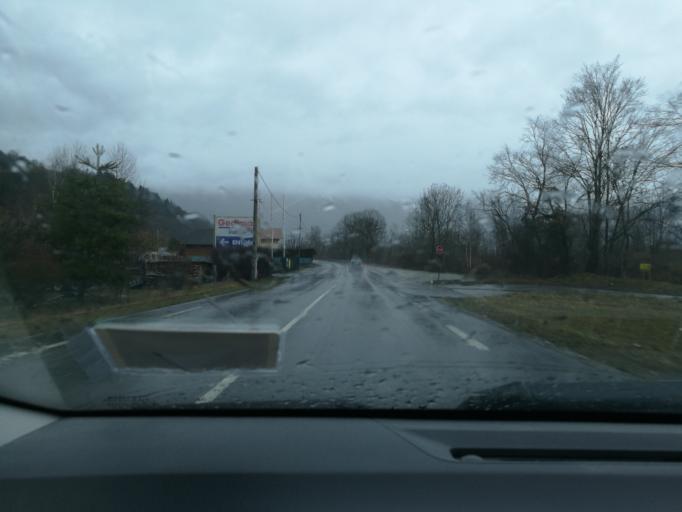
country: FR
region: Rhone-Alpes
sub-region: Departement de la Haute-Savoie
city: Domancy
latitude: 45.9228
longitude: 6.6646
